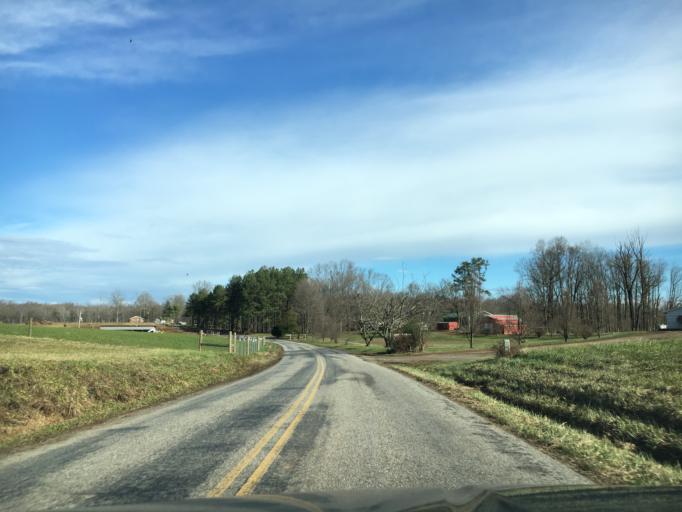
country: US
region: Virginia
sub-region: Amelia County
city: Amelia Court House
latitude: 37.3821
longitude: -78.1261
